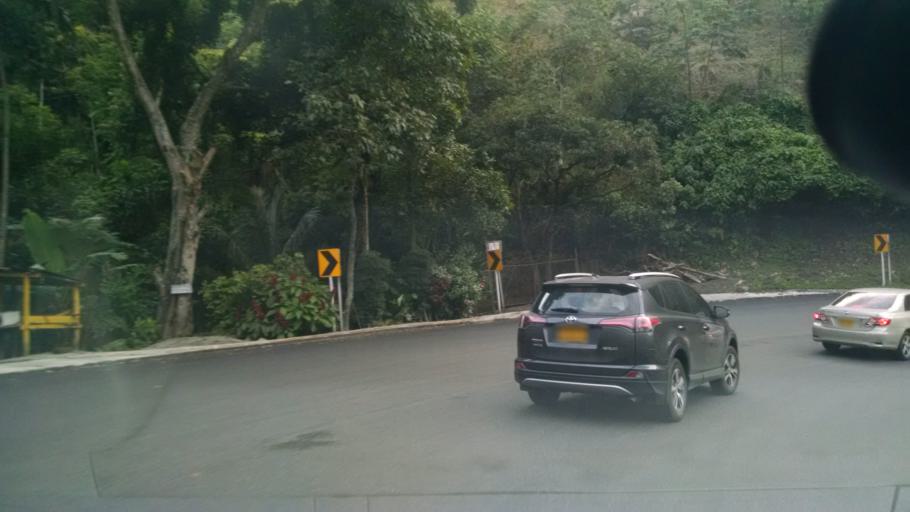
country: CO
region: Antioquia
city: Santa Barbara
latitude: 5.8402
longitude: -75.5789
